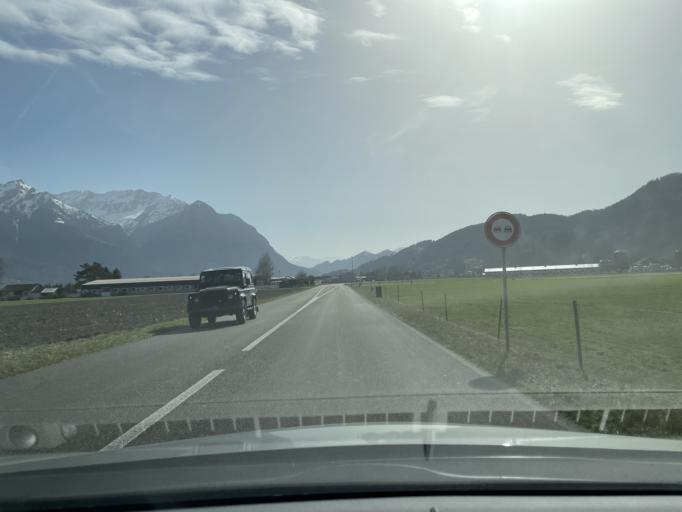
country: CH
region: Saint Gallen
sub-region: Wahlkreis Werdenberg
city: Sevelen
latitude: 47.1369
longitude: 9.4854
